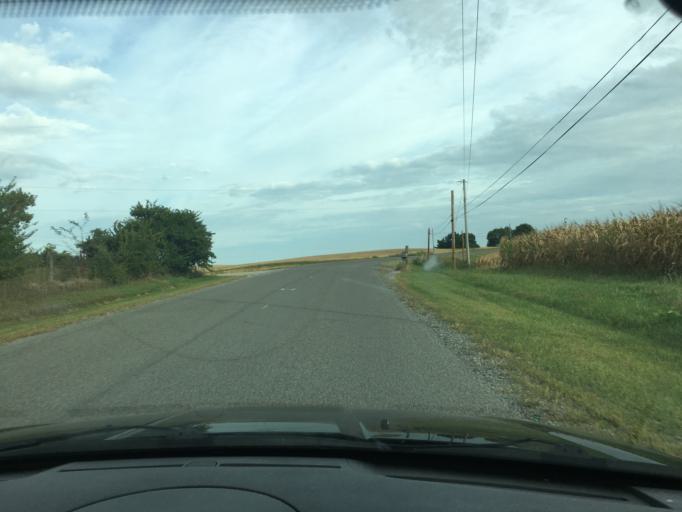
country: US
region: Ohio
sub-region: Logan County
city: West Liberty
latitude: 40.3004
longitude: -83.6867
